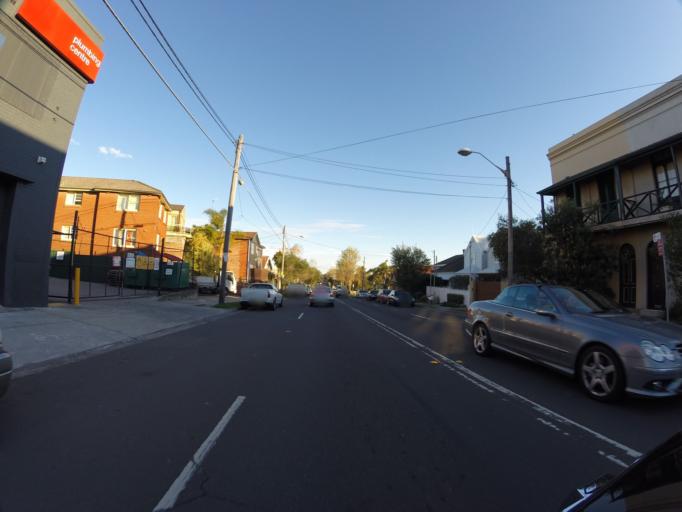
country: AU
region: New South Wales
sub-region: Waverley
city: Bondi Junction
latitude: -33.9014
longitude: 151.2534
